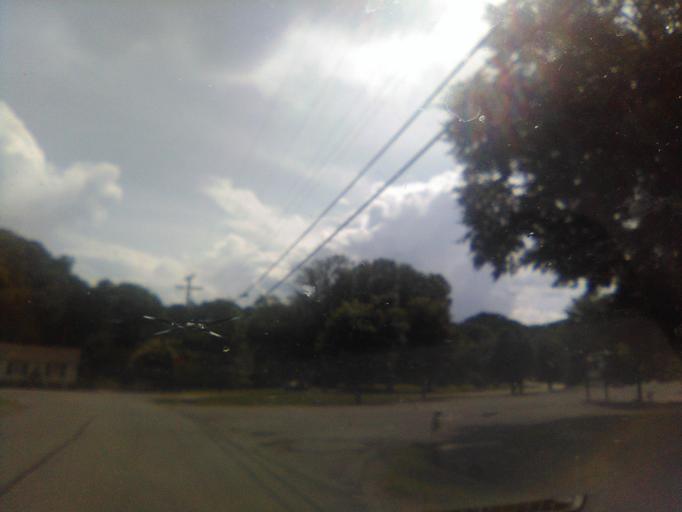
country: US
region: Tennessee
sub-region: Davidson County
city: Belle Meade
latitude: 36.0915
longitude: -86.8922
